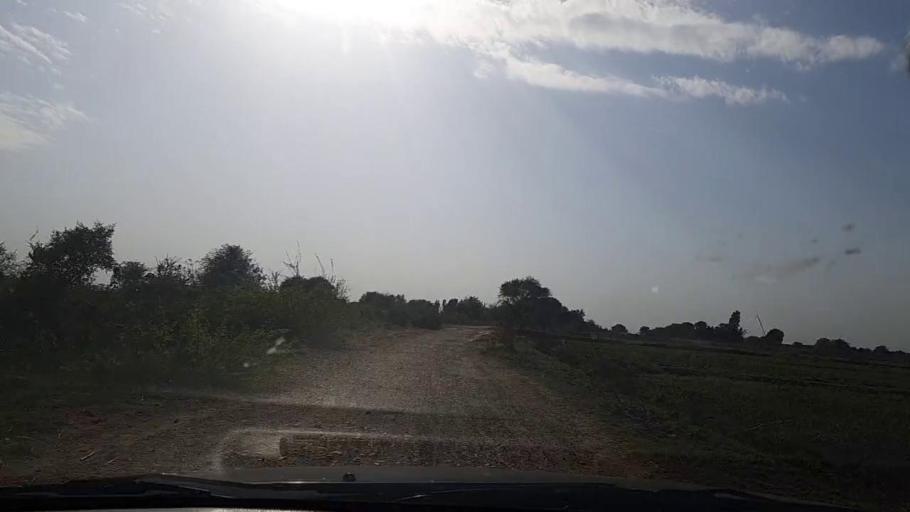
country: PK
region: Sindh
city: Mirpur Batoro
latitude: 24.5529
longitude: 68.1761
